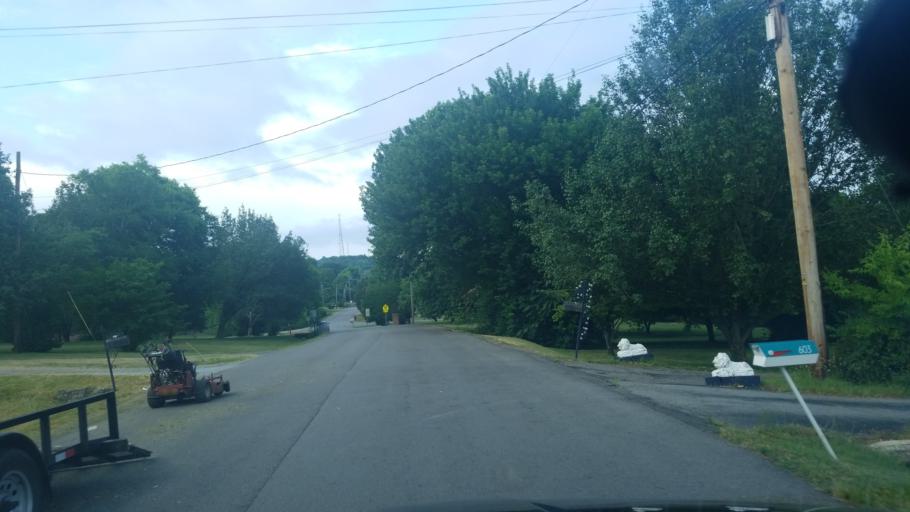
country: US
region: Tennessee
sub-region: Davidson County
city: Nashville
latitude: 36.2338
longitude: -86.7436
